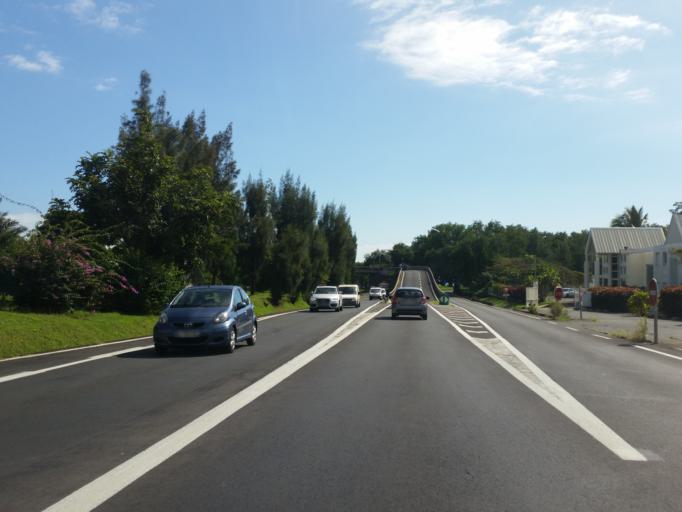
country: RE
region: Reunion
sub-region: Reunion
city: Saint-Denis
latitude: -20.8886
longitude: 55.4901
